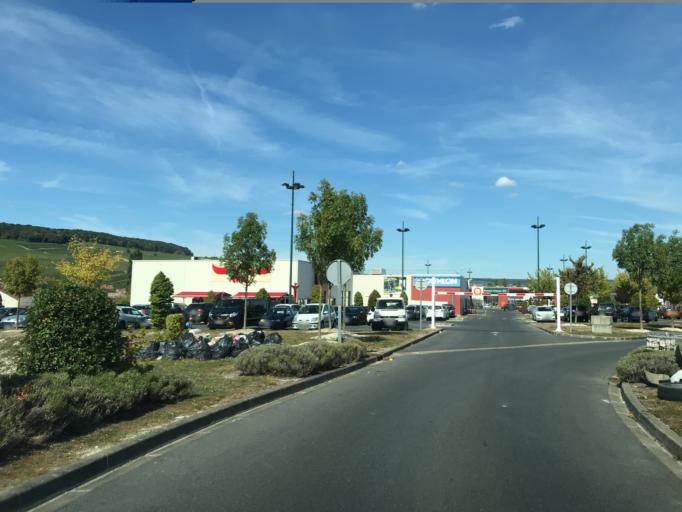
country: FR
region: Champagne-Ardenne
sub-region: Departement de la Marne
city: Pierry
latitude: 49.0234
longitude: 3.9500
